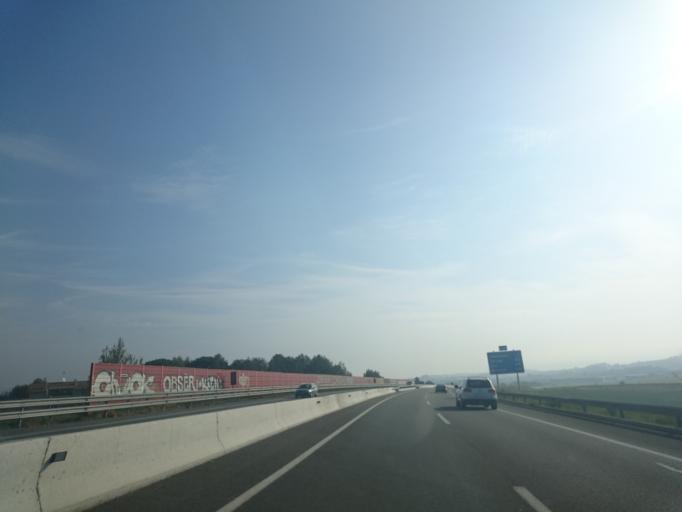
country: ES
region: Catalonia
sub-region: Provincia de Barcelona
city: Sant Fruitos de Bages
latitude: 41.7535
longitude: 1.8465
